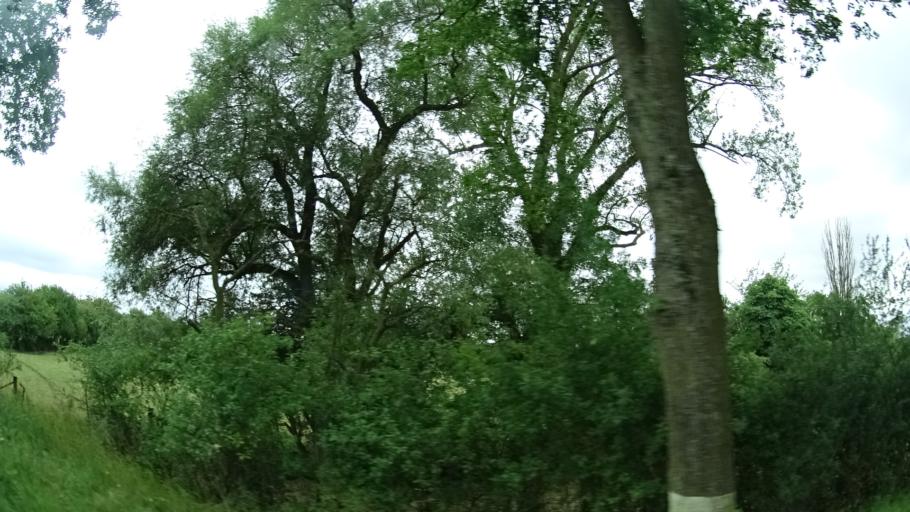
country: LU
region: Grevenmacher
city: Schengen
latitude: 49.4826
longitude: 6.3276
